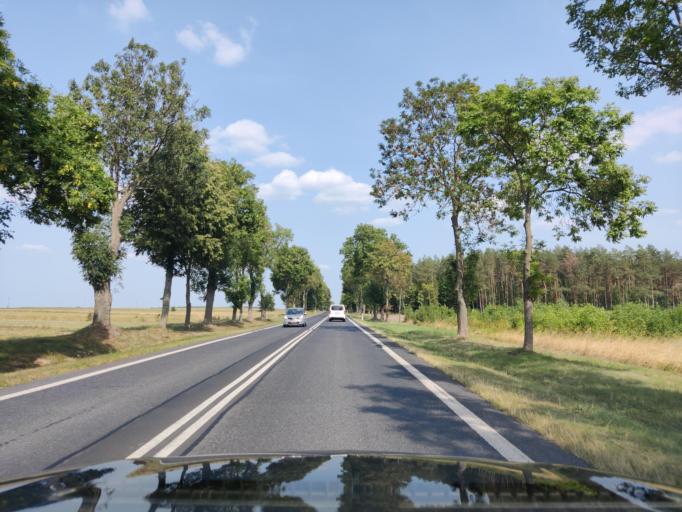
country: PL
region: Masovian Voivodeship
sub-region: Powiat makowski
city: Rzewnie
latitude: 52.8697
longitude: 21.3410
